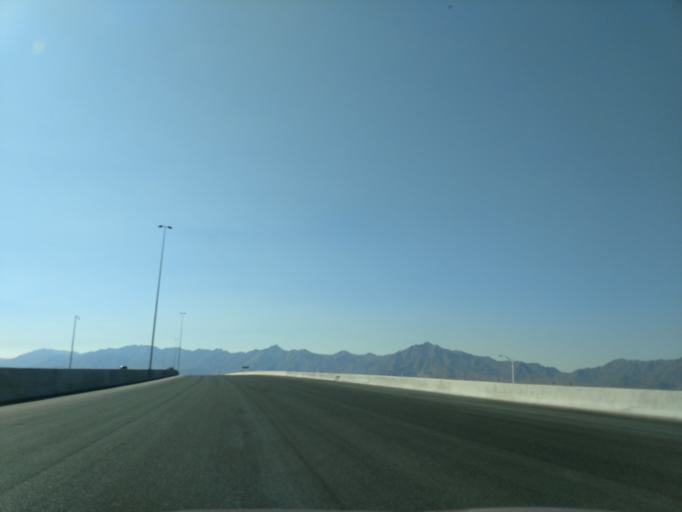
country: US
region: Arizona
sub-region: Maricopa County
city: Laveen
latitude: 33.3655
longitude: -112.1912
